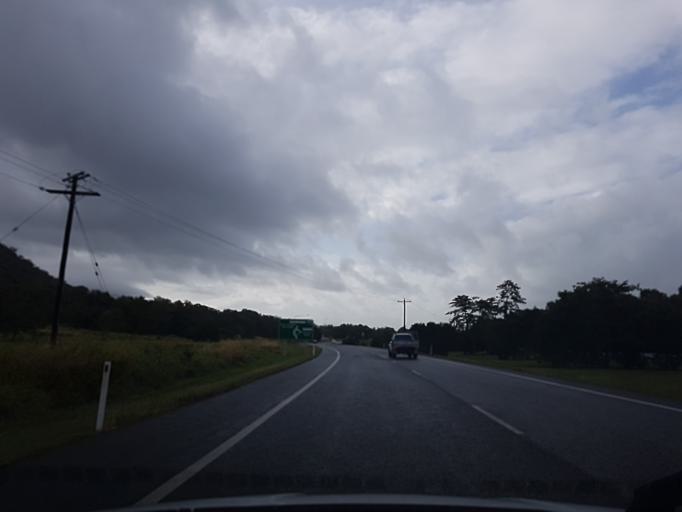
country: AU
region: Queensland
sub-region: Cairns
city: Trinity Beach
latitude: -16.8148
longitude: 145.6933
